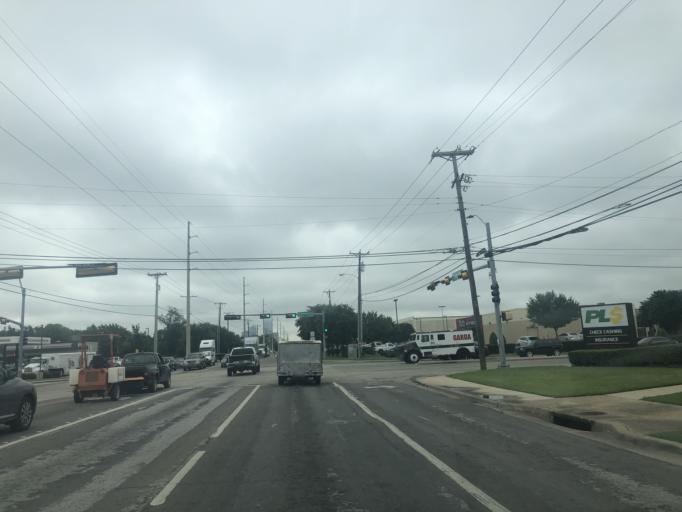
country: US
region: Texas
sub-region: Dallas County
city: Dallas
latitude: 32.7786
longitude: -96.8570
